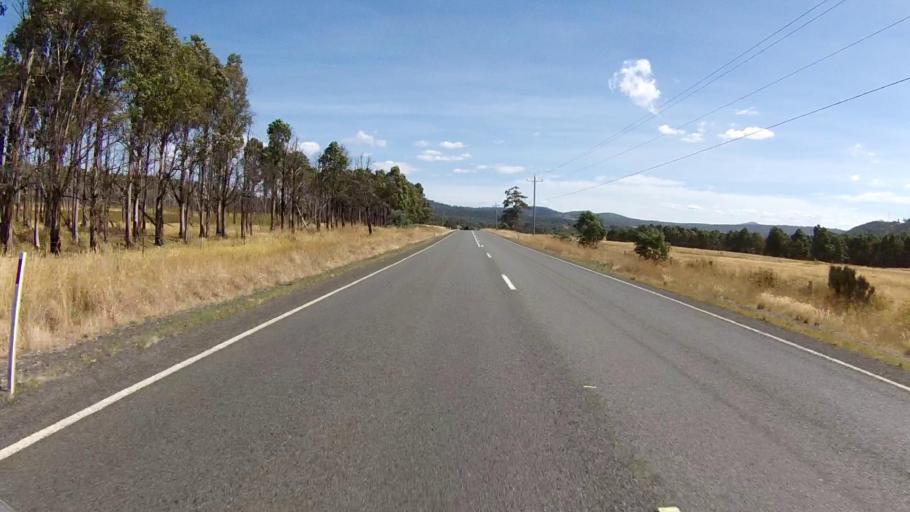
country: AU
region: Tasmania
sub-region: Sorell
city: Sorell
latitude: -42.6063
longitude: 147.7429
